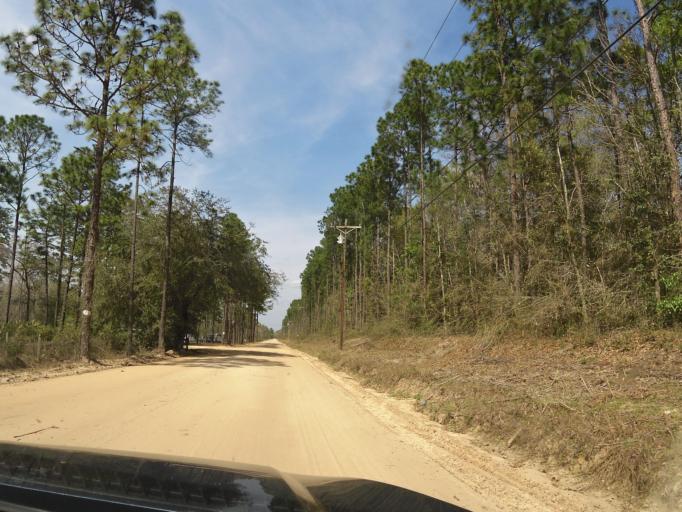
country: US
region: Florida
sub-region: Clay County
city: Middleburg
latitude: 30.1208
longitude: -81.8818
